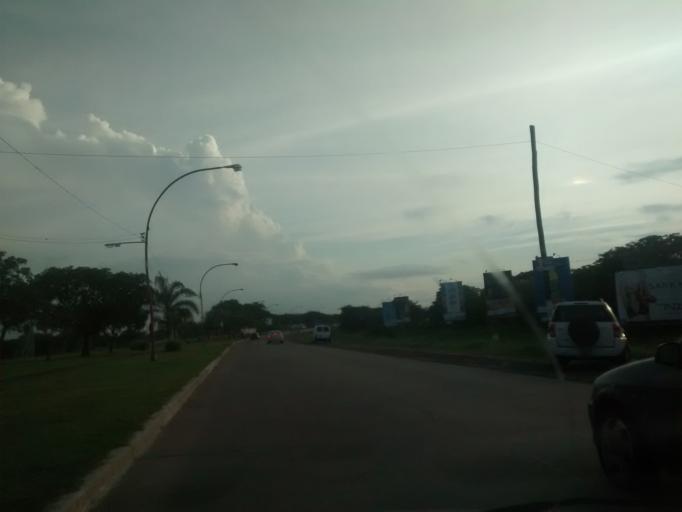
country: AR
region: Chaco
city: Resistencia
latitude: -27.4259
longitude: -58.9600
